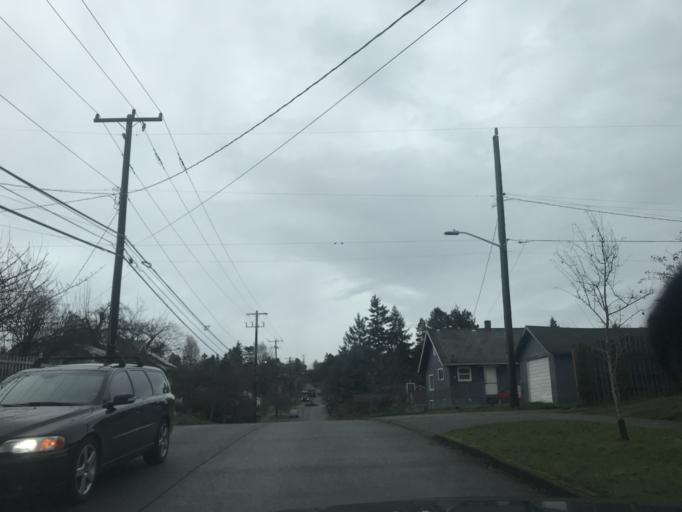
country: US
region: Washington
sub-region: King County
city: White Center
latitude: 47.5283
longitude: -122.3588
